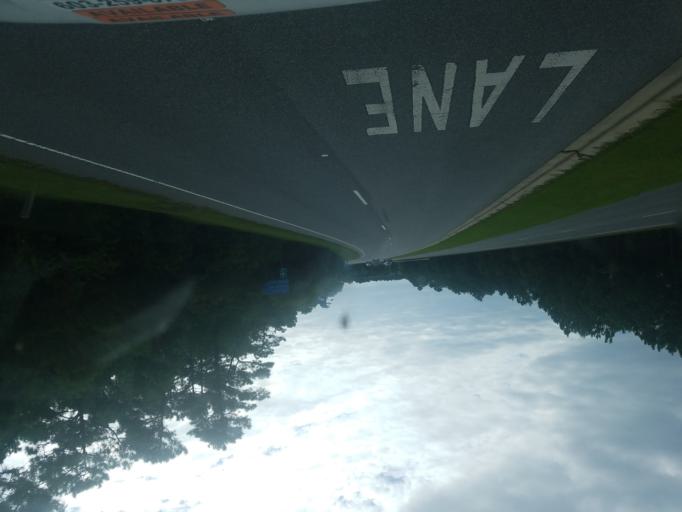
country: US
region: North Carolina
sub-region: Dare County
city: Manteo
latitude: 35.8889
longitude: -75.6642
